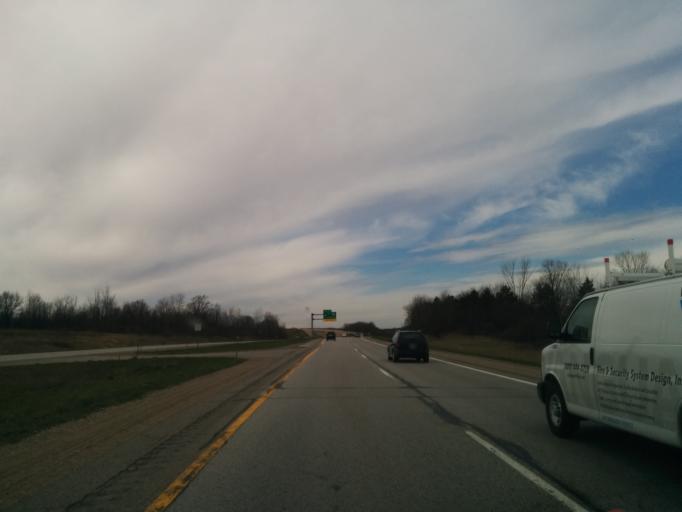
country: US
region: Michigan
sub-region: Ottawa County
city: Jenison
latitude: 42.8650
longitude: -85.8063
